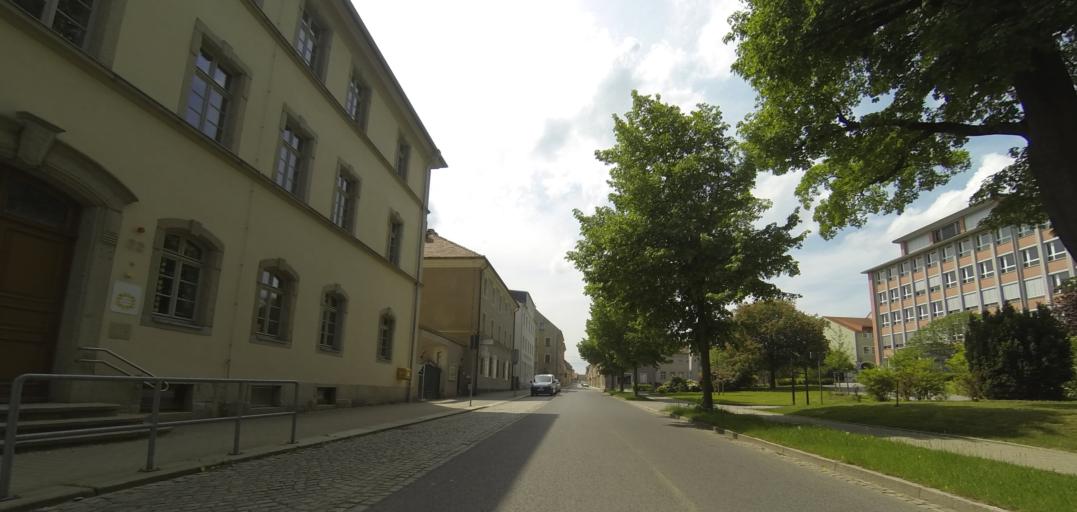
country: DE
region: Saxony
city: Bischofswerda
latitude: 51.1299
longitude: 14.1831
